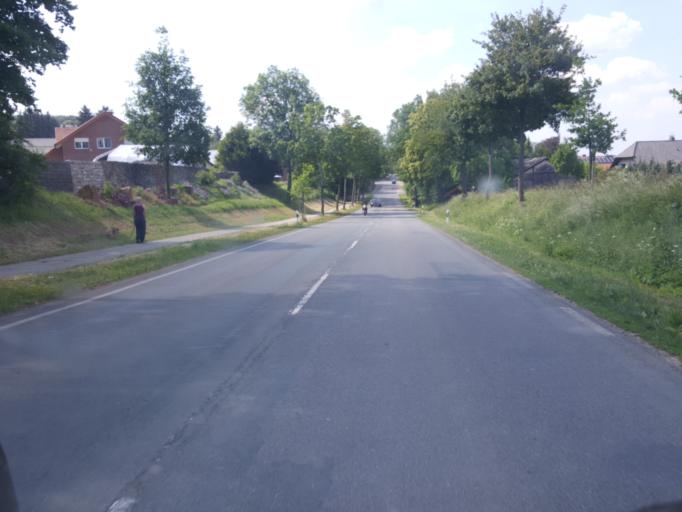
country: DE
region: North Rhine-Westphalia
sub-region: Regierungsbezirk Detmold
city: Hille
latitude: 52.2788
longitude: 8.7657
